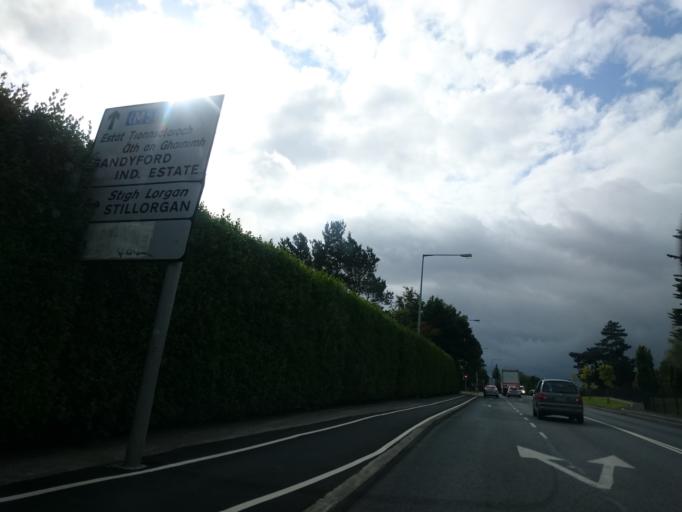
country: IE
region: Leinster
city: Sandyford
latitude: 53.2898
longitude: -6.2271
